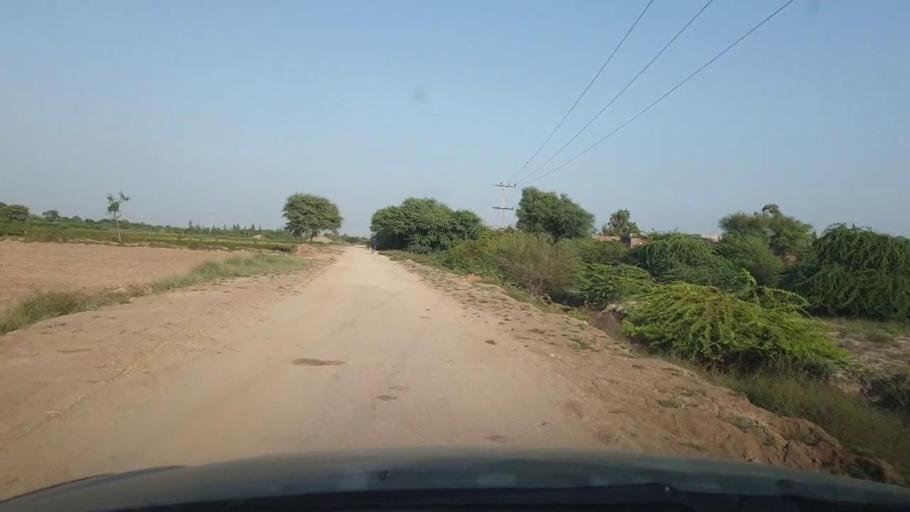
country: PK
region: Sindh
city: Tando Ghulam Ali
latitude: 25.1645
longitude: 68.9559
